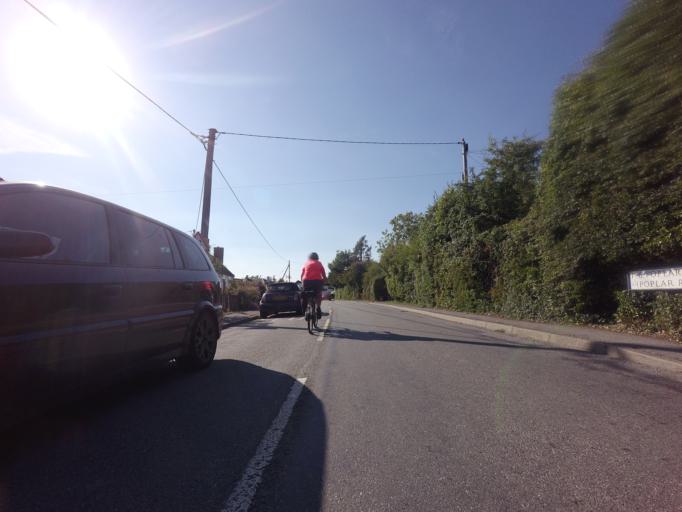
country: GB
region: England
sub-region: Kent
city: Tenterden
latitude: 51.0158
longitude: 0.7050
